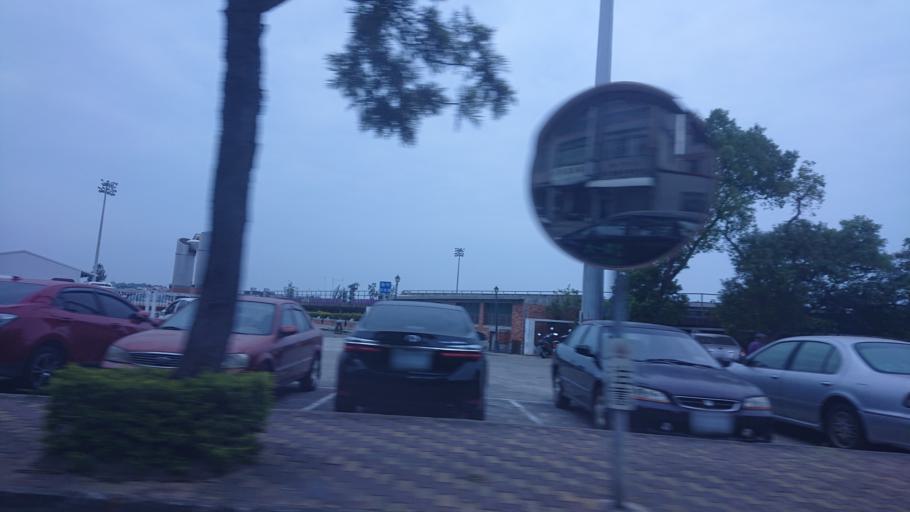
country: TW
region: Fukien
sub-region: Kinmen
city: Jincheng
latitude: 24.4308
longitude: 118.3139
